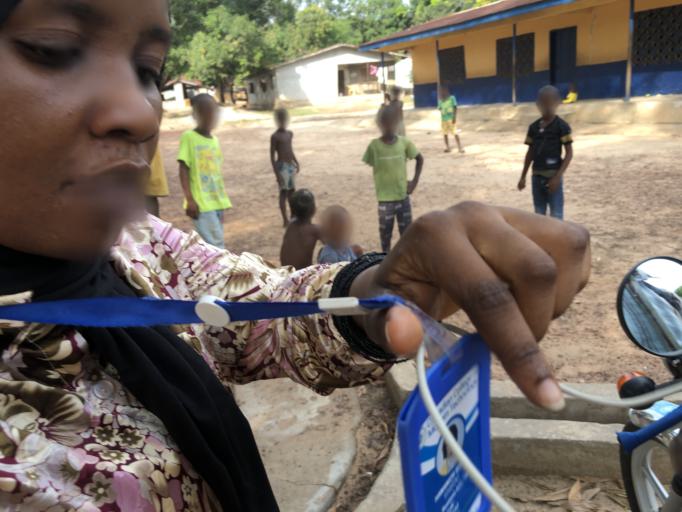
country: SL
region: Northern Province
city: Yonibana
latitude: 8.4619
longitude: -12.2063
